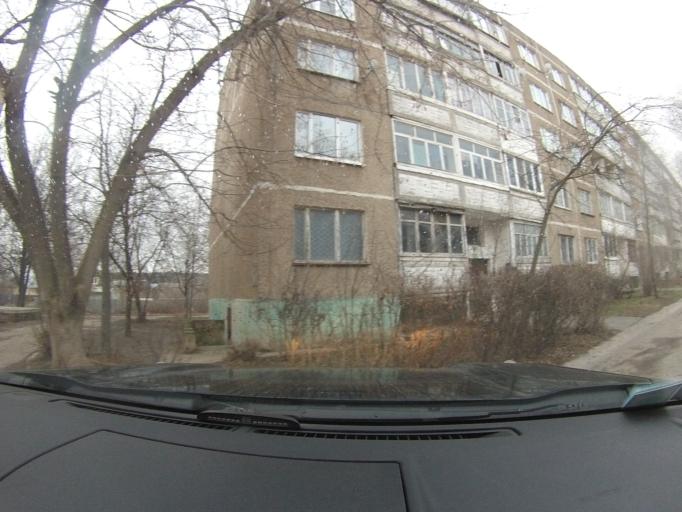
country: RU
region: Moskovskaya
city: Peski
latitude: 55.2497
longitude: 38.7666
